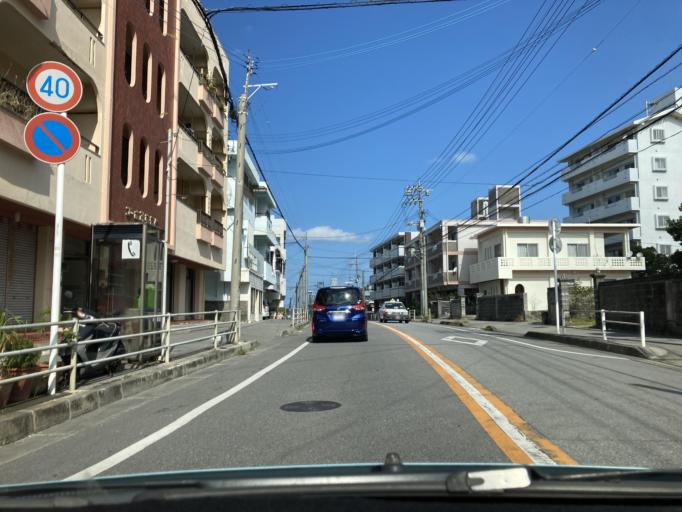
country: JP
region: Okinawa
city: Tomigusuku
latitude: 26.1844
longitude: 127.6819
